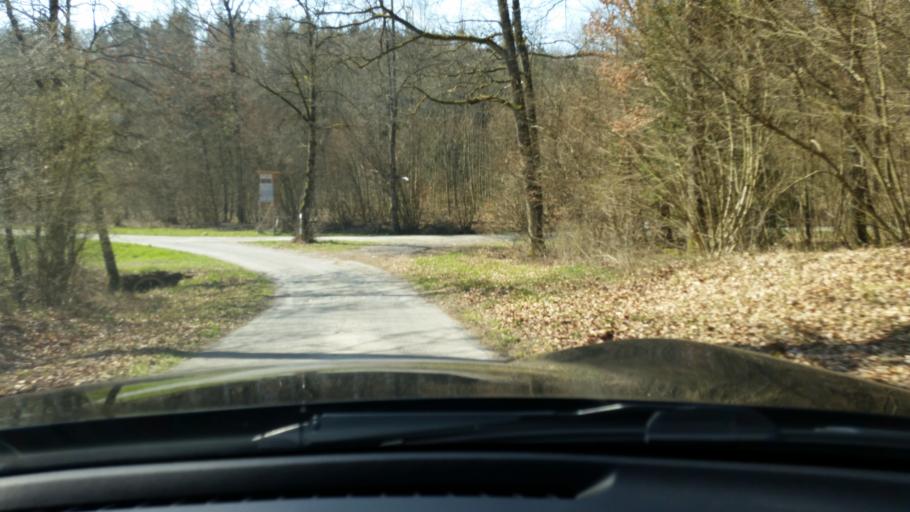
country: DE
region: Baden-Wuerttemberg
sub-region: Karlsruhe Region
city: Rosenberg
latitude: 49.4207
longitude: 9.4969
